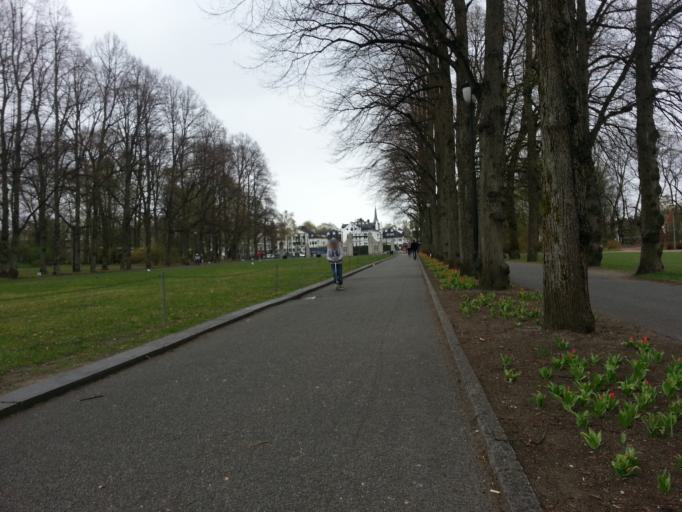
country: NO
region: Oslo
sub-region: Oslo
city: Sjolyststranda
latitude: 59.9255
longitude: 10.7050
